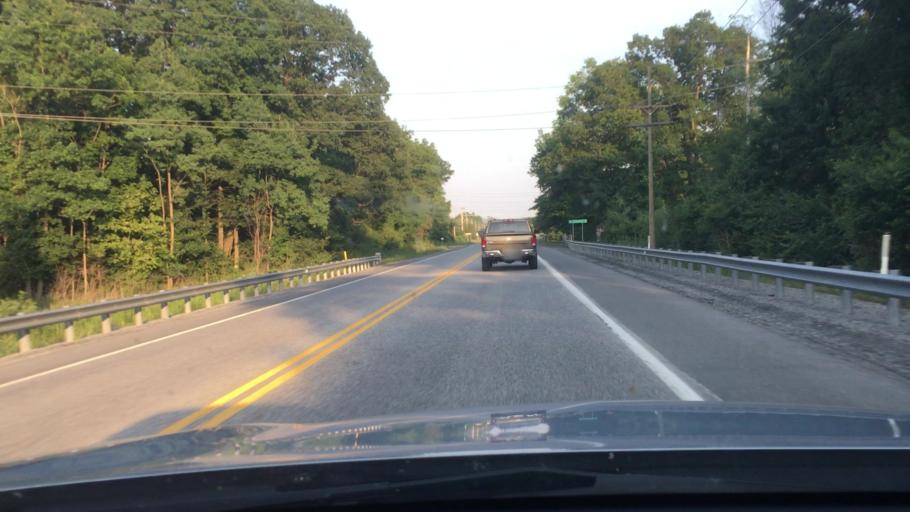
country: US
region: Pennsylvania
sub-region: York County
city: Dillsburg
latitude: 40.0920
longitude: -76.9540
